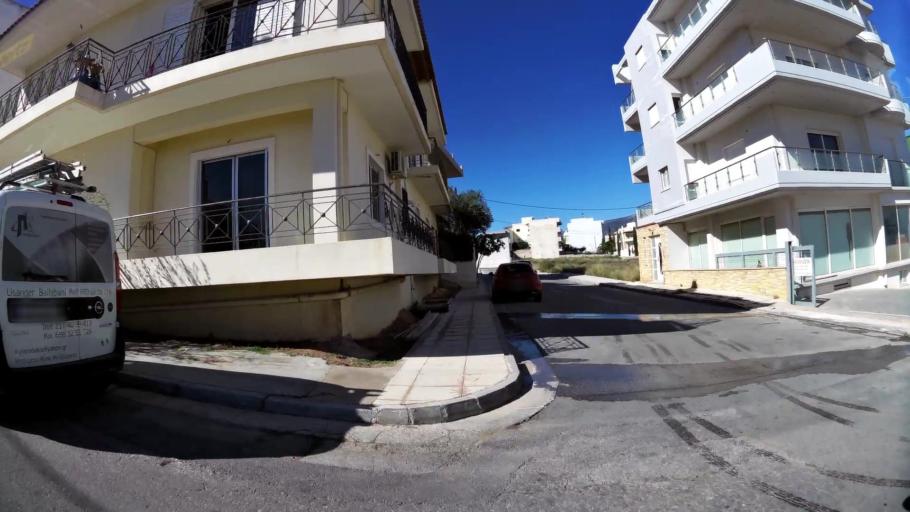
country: GR
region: Attica
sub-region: Nomarchia Anatolikis Attikis
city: Koropi
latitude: 37.9021
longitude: 23.8827
